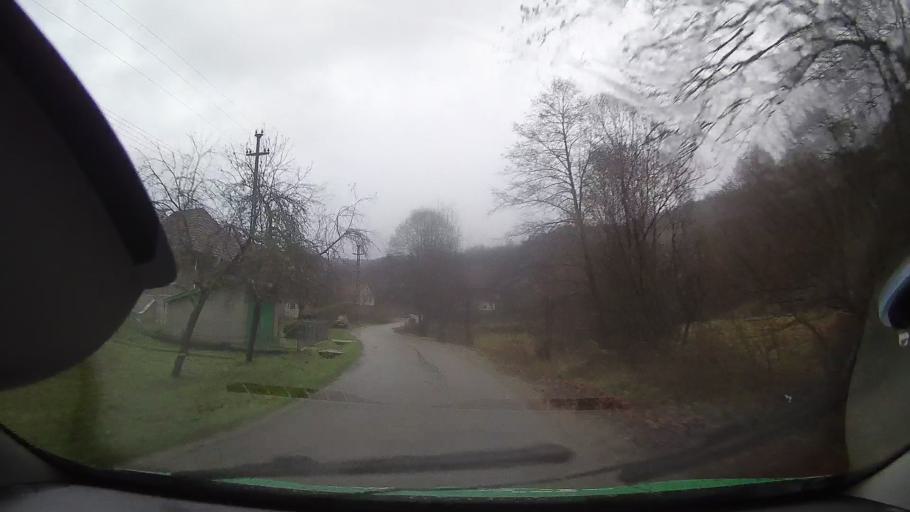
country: RO
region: Alba
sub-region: Comuna Avram Iancu
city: Avram Iancu
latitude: 46.2994
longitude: 22.7598
